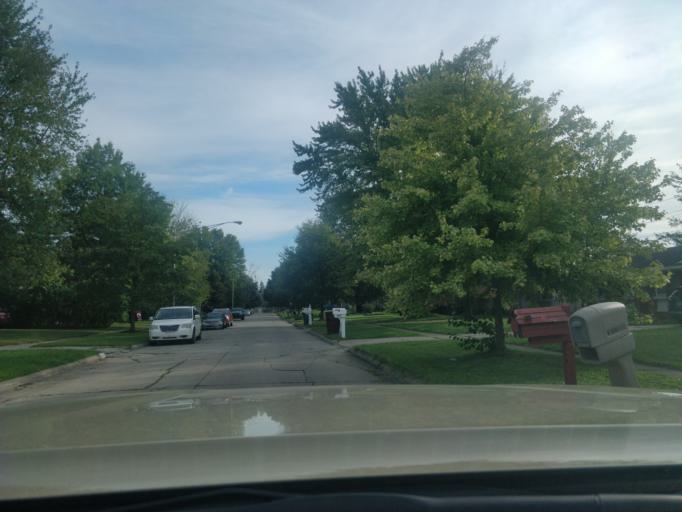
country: US
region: Michigan
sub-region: Wayne County
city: Belleville
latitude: 42.2245
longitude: -83.4535
